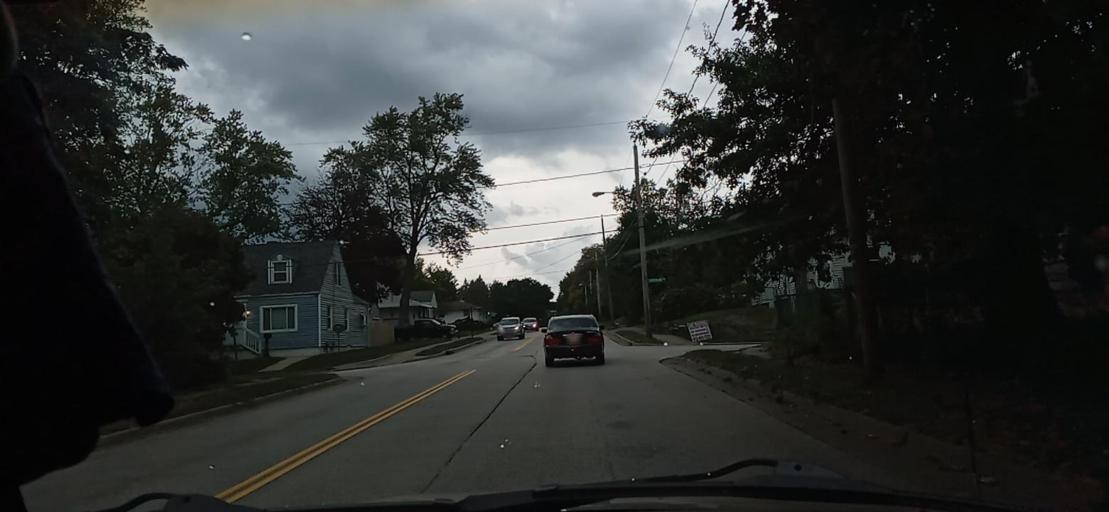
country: US
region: Ohio
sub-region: Summit County
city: Akron
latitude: 41.0637
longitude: -81.5583
